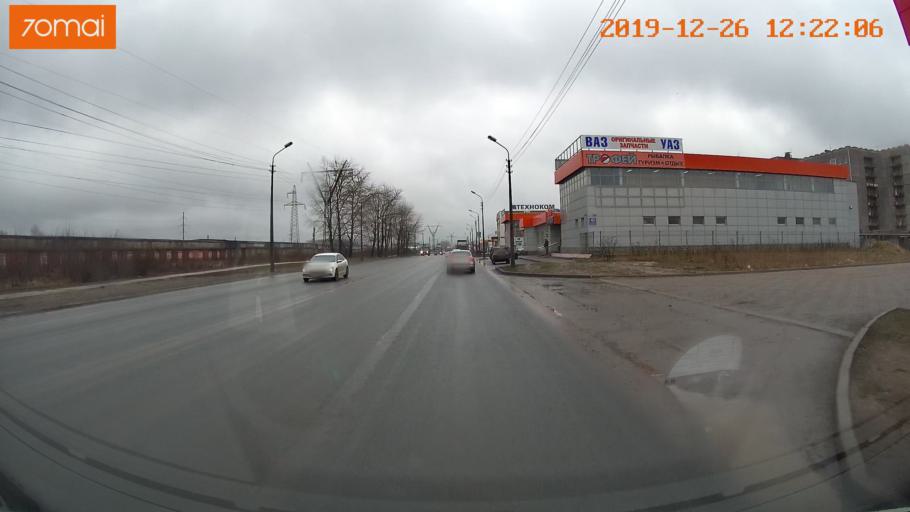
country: RU
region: Vologda
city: Tonshalovo
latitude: 59.1510
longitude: 37.9409
